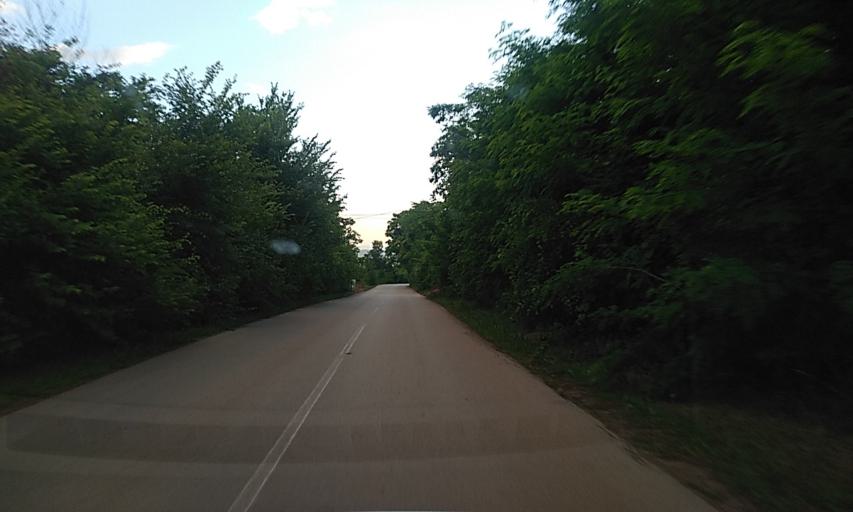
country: RS
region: Central Serbia
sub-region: Nisavski Okrug
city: Niska Banja
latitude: 43.3681
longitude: 21.9837
